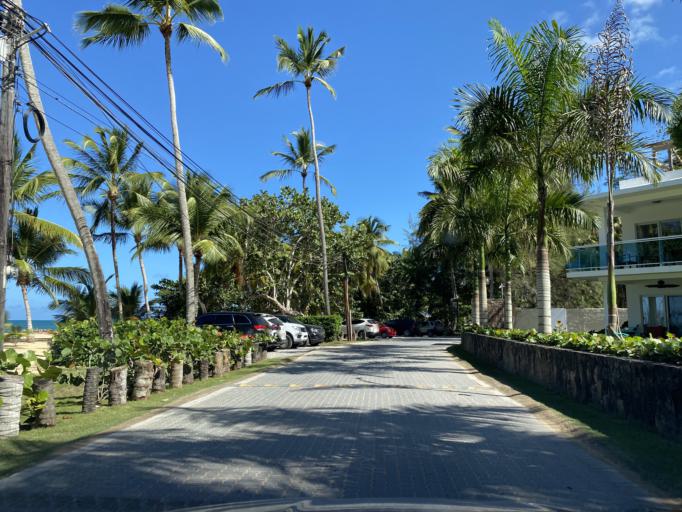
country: DO
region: Samana
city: Las Terrenas
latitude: 19.3257
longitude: -69.5508
